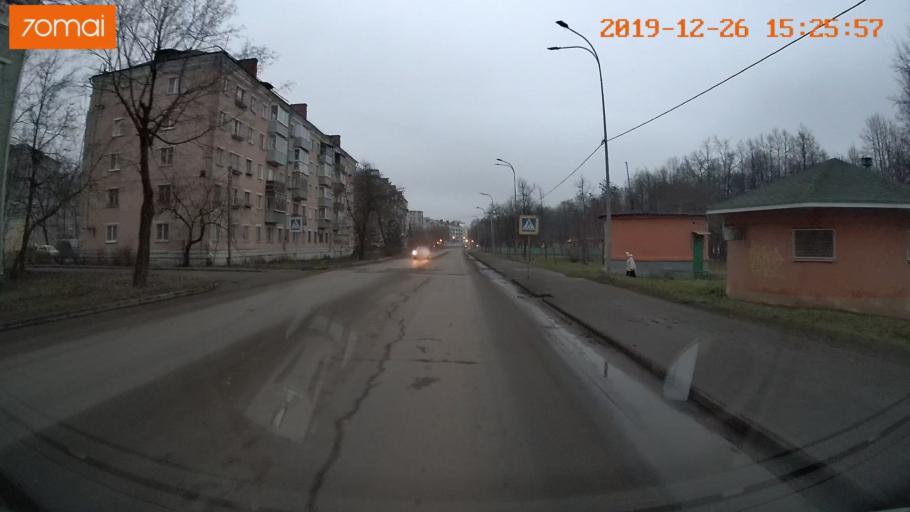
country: RU
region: Jaroslavl
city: Rybinsk
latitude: 58.0553
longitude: 38.8331
